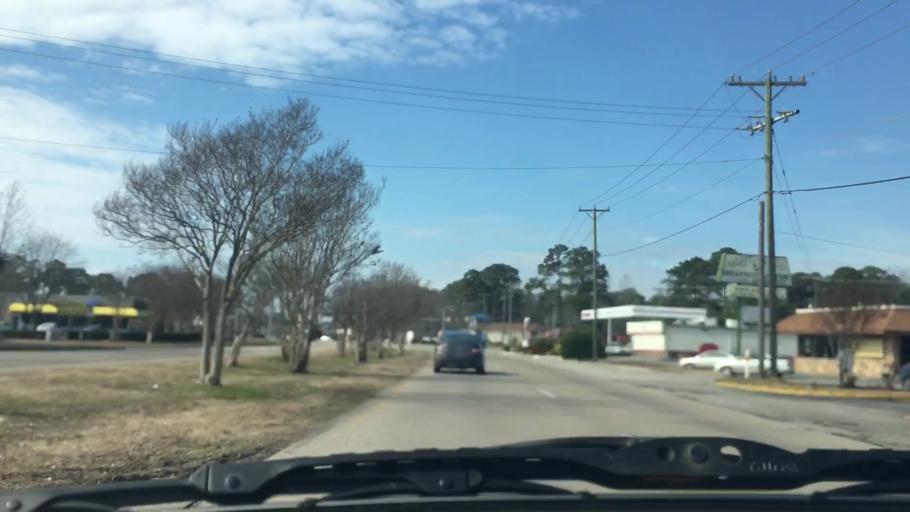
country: US
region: Virginia
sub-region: City of Portsmouth
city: Portsmouth Heights
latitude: 36.8647
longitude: -76.4080
